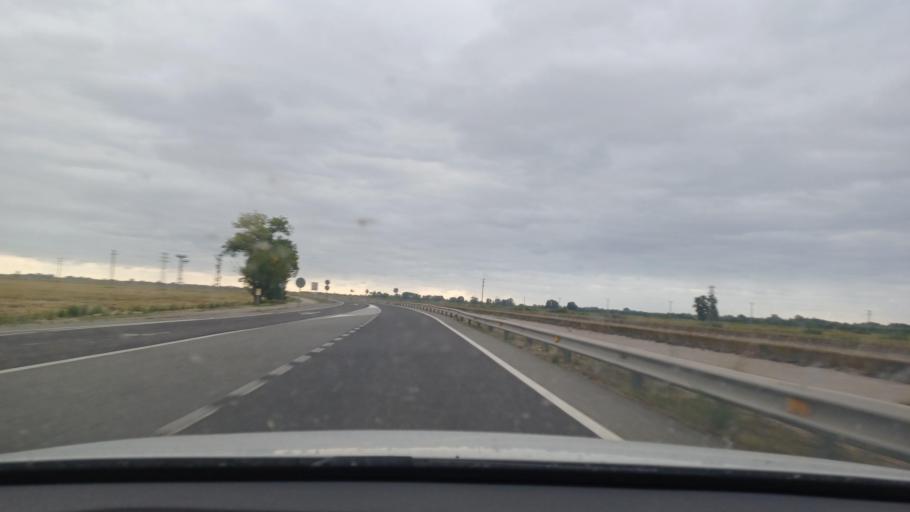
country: ES
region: Catalonia
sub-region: Provincia de Tarragona
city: Amposta
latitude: 40.7136
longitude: 0.5954
